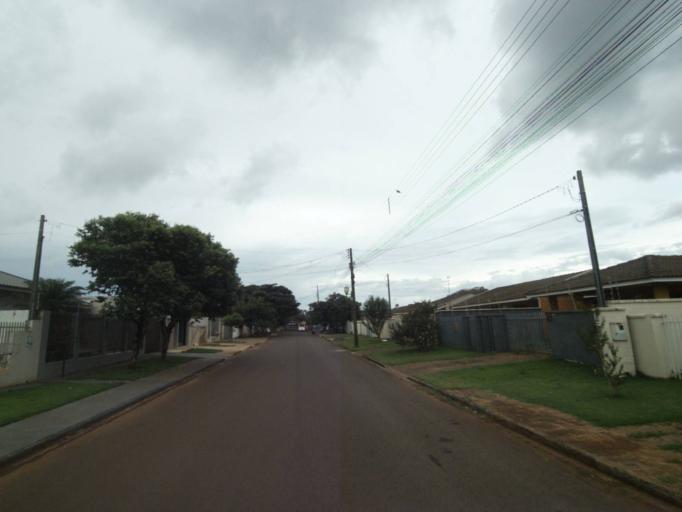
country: BR
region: Parana
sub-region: Campo Mourao
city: Campo Mourao
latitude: -24.0218
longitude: -52.3577
